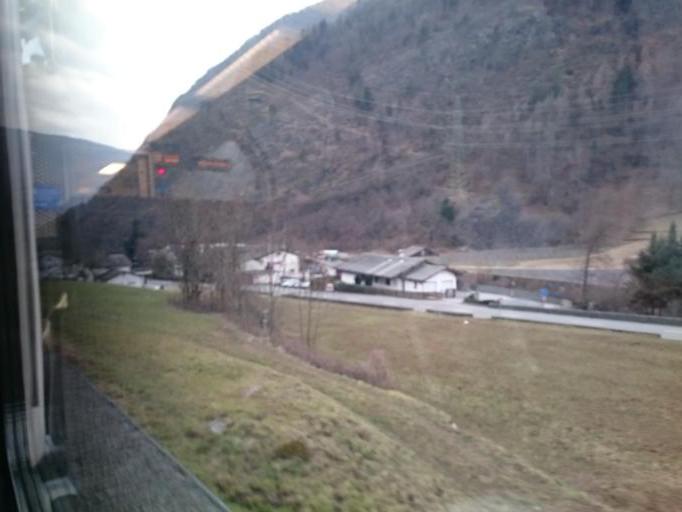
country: CH
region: Grisons
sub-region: Bernina District
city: Brusio
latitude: 46.2398
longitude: 10.1359
